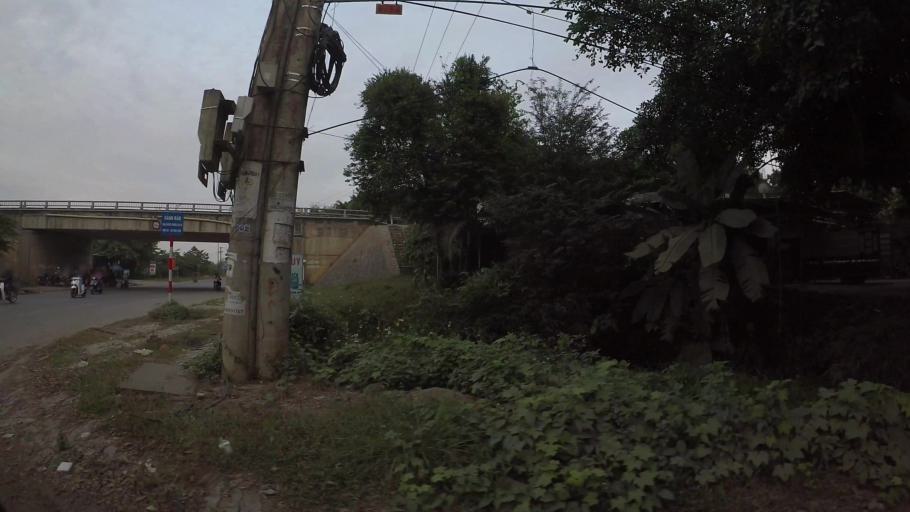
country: VN
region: Da Nang
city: Lien Chieu
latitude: 16.0595
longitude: 108.0975
